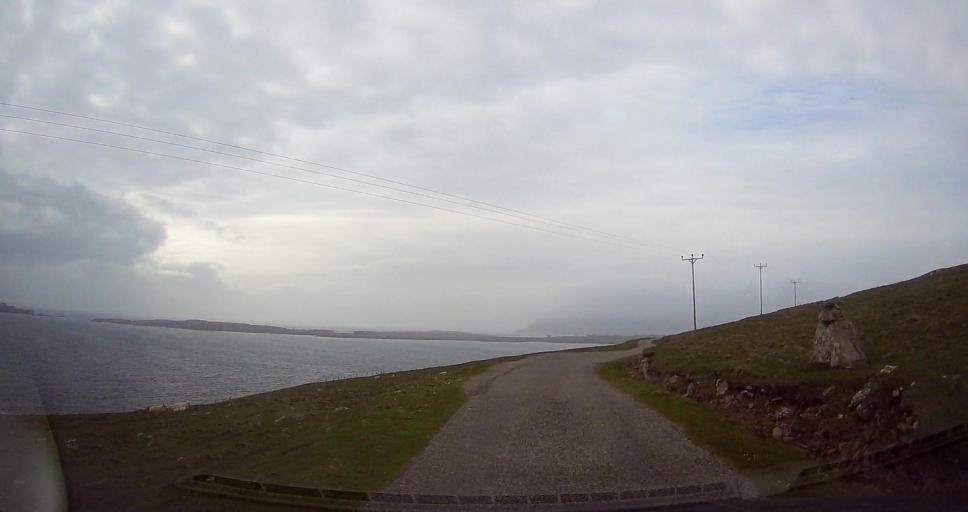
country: GB
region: Scotland
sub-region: Shetland Islands
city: Sandwick
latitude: 59.8587
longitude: -1.2753
